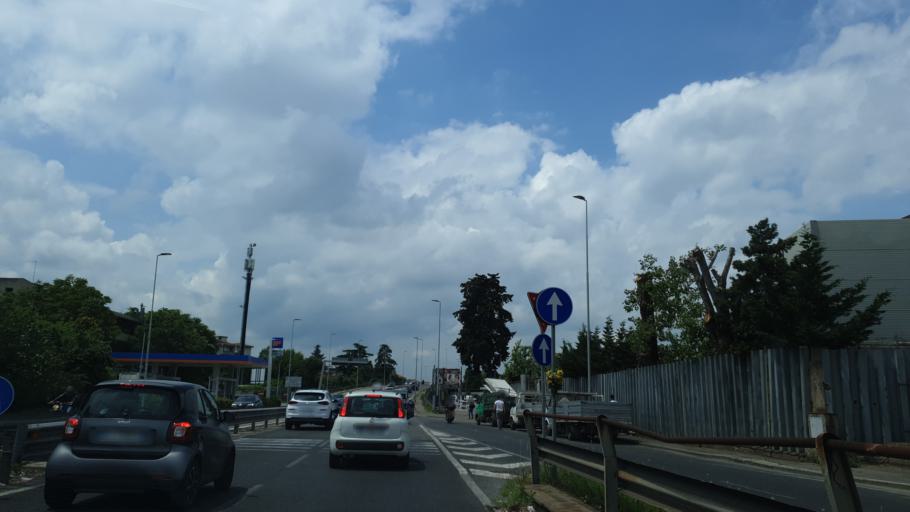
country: IT
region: Tuscany
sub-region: Province of Florence
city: Scandicci
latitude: 43.7730
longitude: 11.2111
